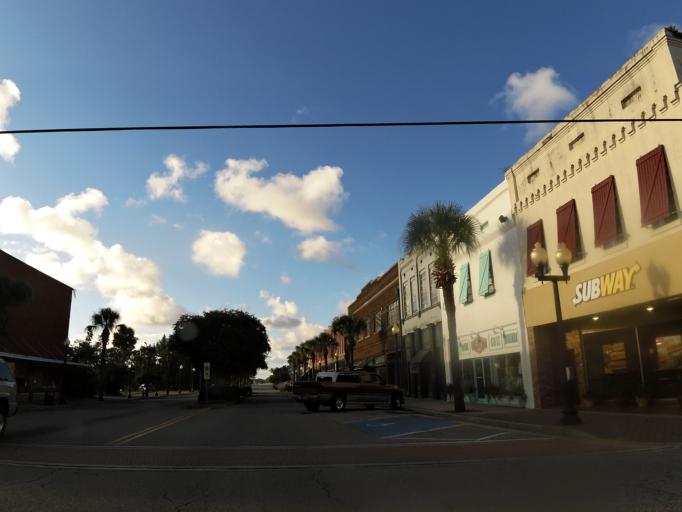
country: US
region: Georgia
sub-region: Glynn County
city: Brunswick
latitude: 31.1504
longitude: -81.4958
